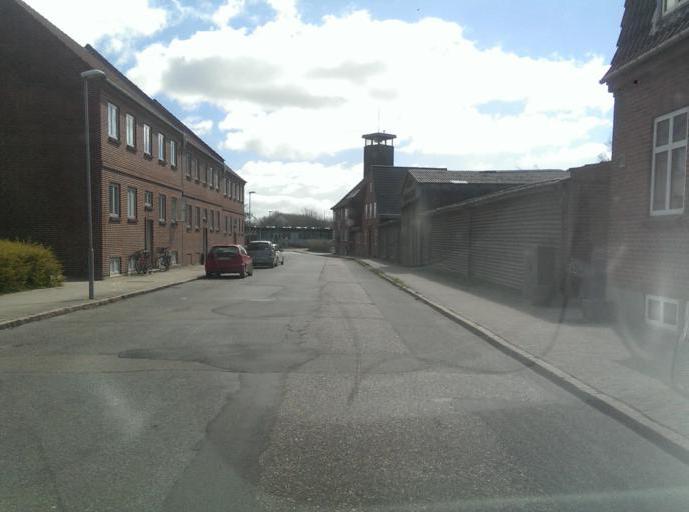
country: DK
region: South Denmark
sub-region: Esbjerg Kommune
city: Esbjerg
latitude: 55.4648
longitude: 8.4626
